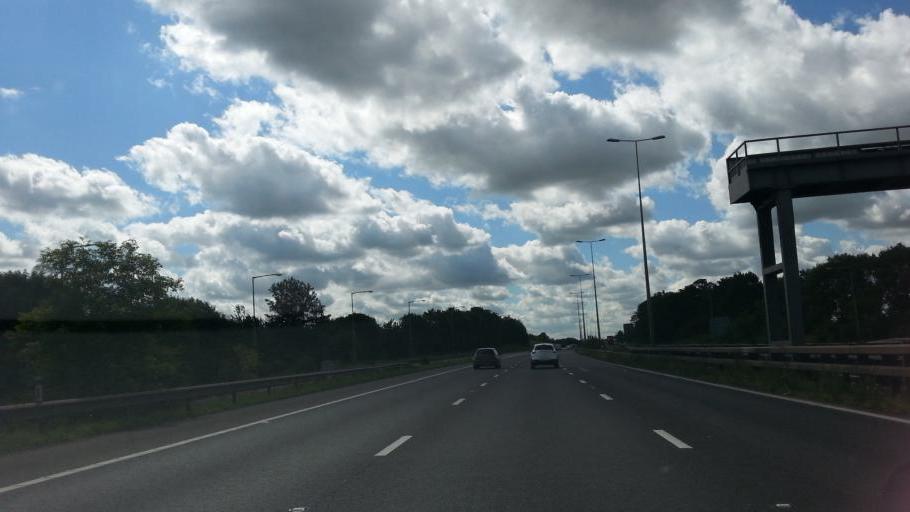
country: GB
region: England
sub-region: Leicestershire
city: Enderby
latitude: 52.5986
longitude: -1.1947
